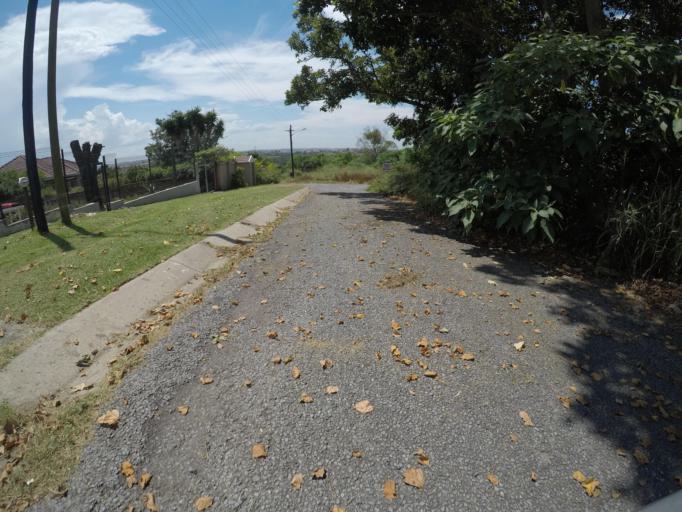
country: ZA
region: Eastern Cape
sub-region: Buffalo City Metropolitan Municipality
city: East London
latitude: -33.0308
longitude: 27.8665
